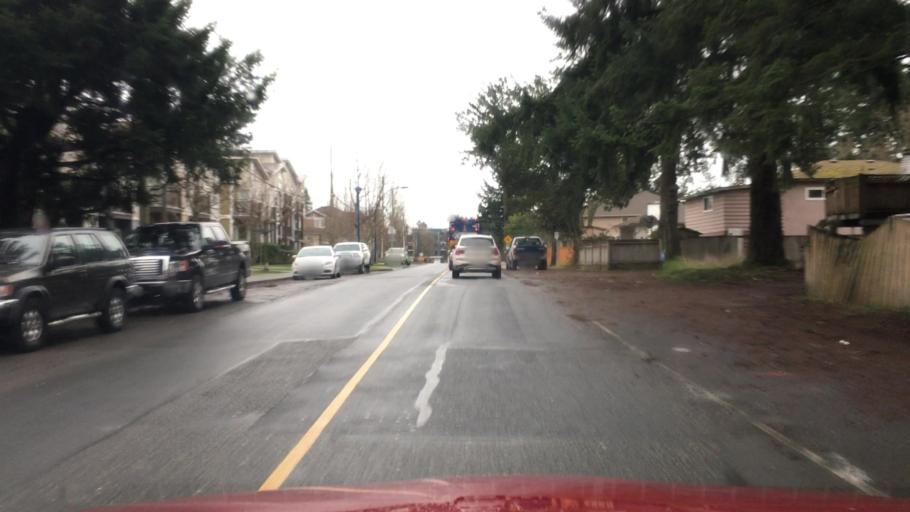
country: CA
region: British Columbia
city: Langford
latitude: 48.4536
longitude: -123.5028
